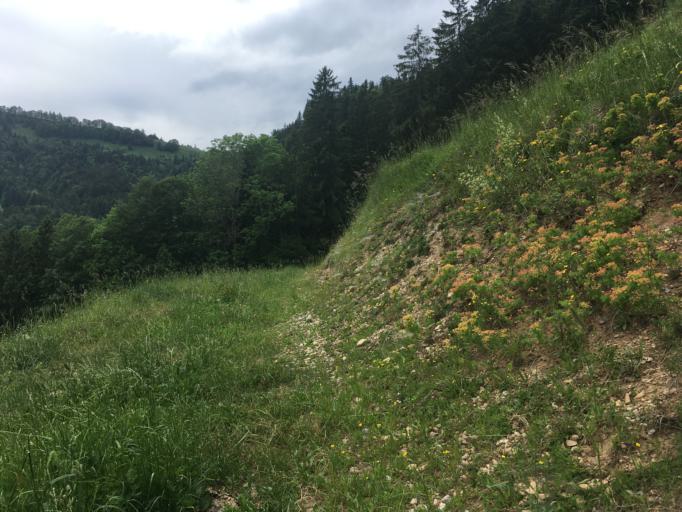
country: CH
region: Saint Gallen
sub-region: Wahlkreis Toggenburg
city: Lichtensteig
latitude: 47.3202
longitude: 9.0489
